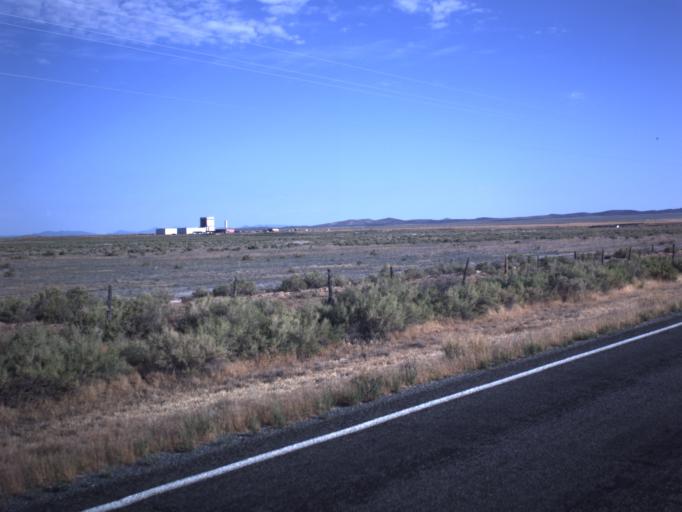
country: US
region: Utah
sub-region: Iron County
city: Enoch
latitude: 37.8688
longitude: -113.0316
